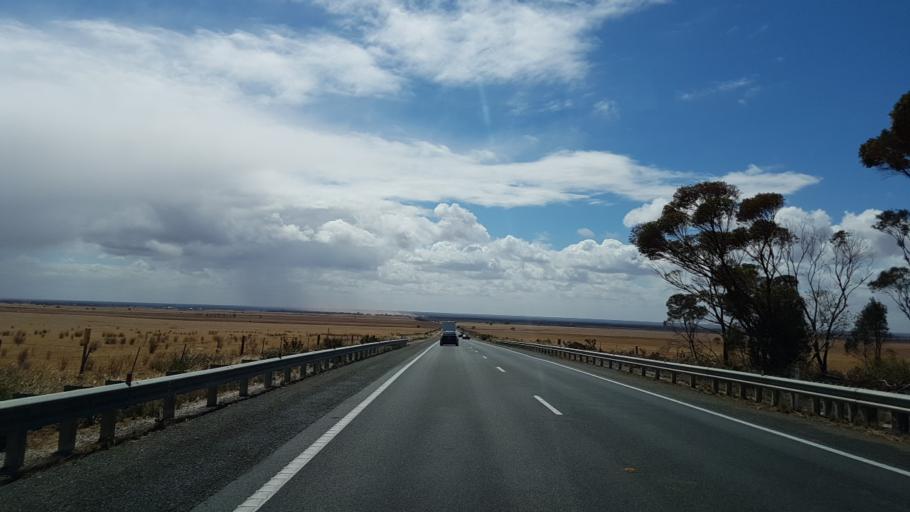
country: AU
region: South Australia
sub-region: Barossa
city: Angaston
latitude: -34.4025
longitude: 139.2410
